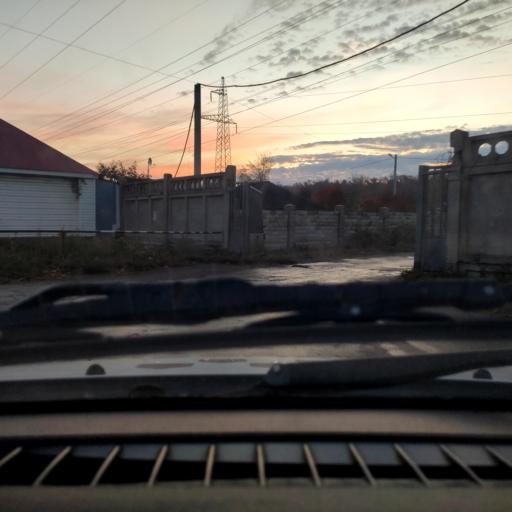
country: RU
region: Samara
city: Zhigulevsk
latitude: 53.5175
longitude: 49.4795
